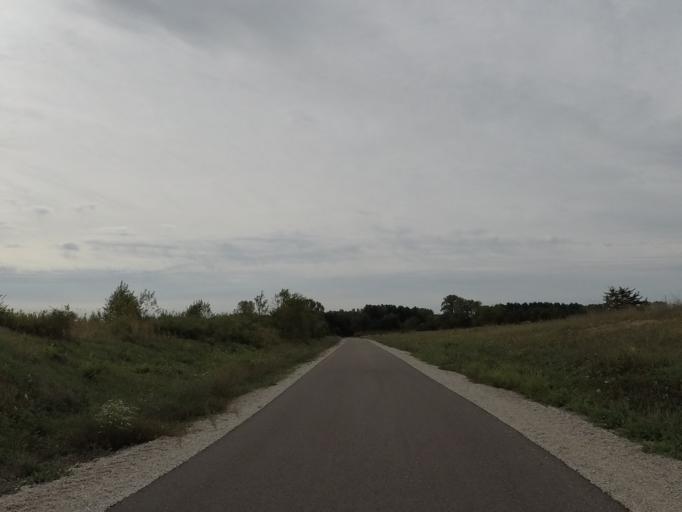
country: US
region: Wisconsin
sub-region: Sauk County
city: Prairie du Sac
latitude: 43.3656
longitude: -89.7398
